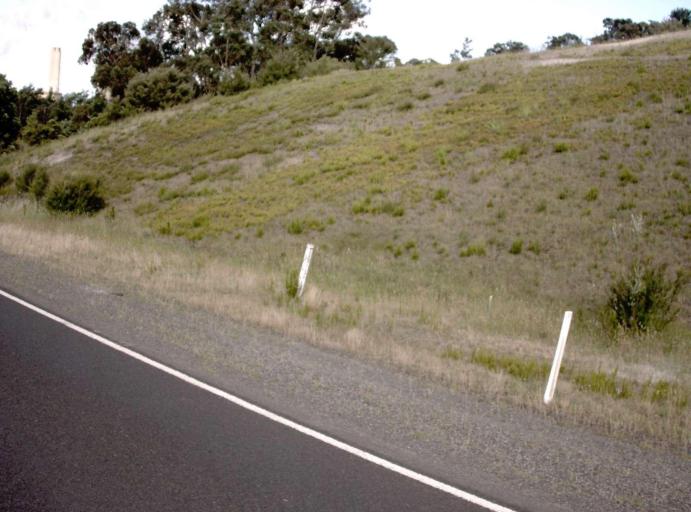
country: AU
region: Victoria
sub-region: Latrobe
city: Moe
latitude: -38.1825
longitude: 146.3292
